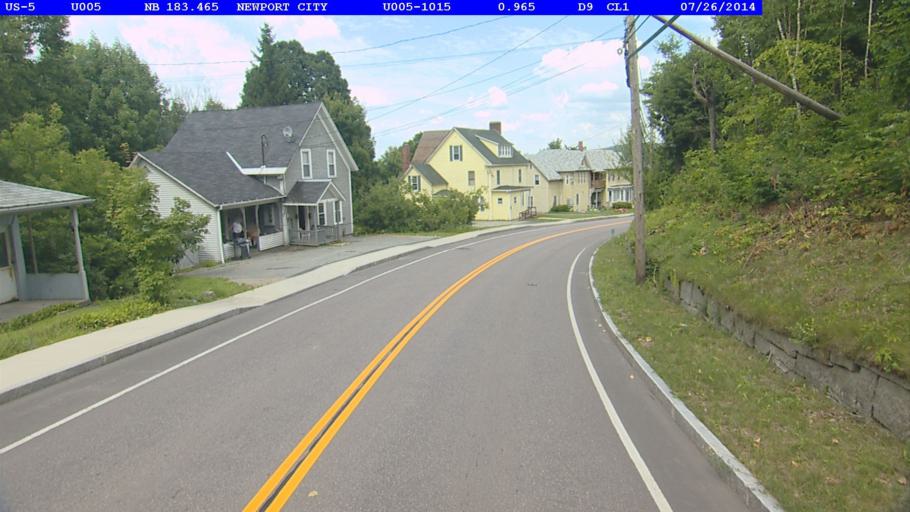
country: US
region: Vermont
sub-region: Orleans County
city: Newport
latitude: 44.9321
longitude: -72.2150
